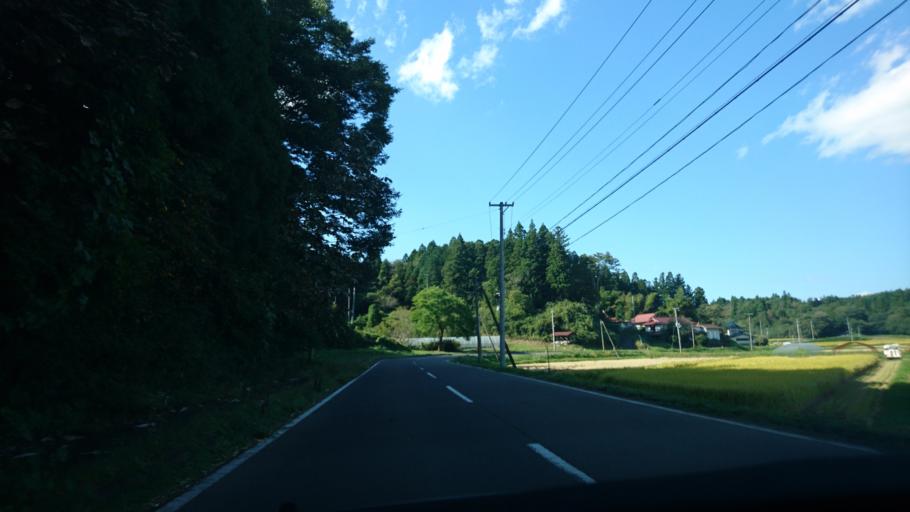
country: JP
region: Iwate
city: Ichinoseki
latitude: 38.8633
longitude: 141.0458
